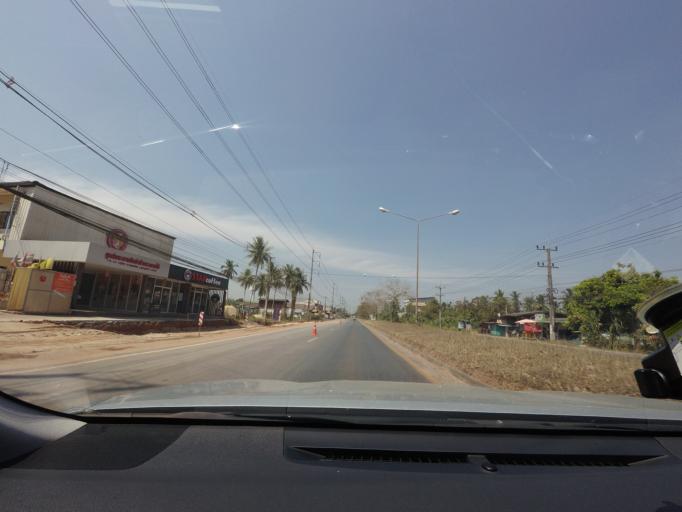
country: TH
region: Surat Thani
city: Kanchanadit
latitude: 9.1473
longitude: 99.4070
